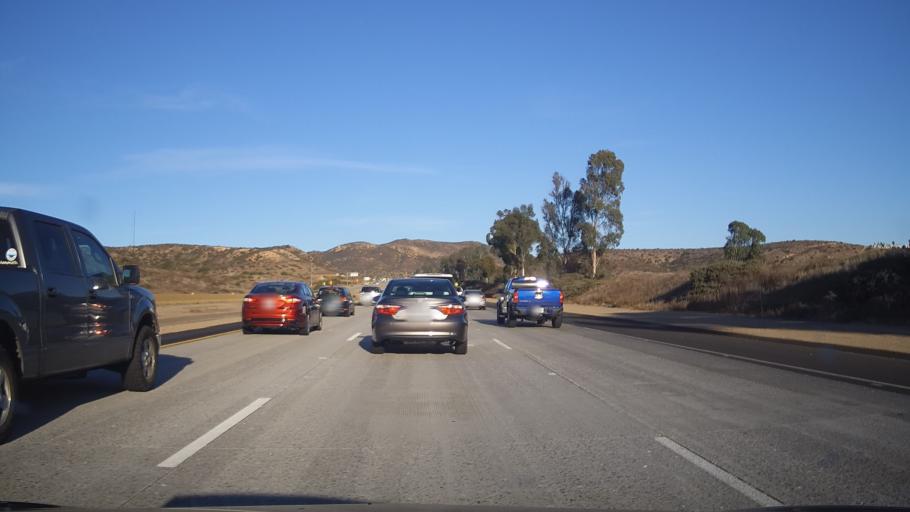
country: US
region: California
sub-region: San Diego County
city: La Mesa
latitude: 32.8407
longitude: -117.0923
